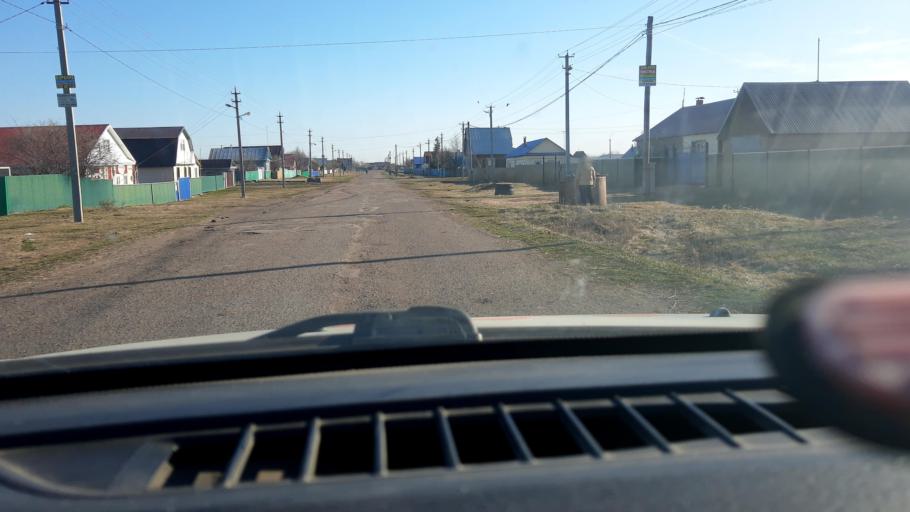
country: RU
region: Bashkortostan
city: Asanovo
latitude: 54.9057
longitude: 55.4895
